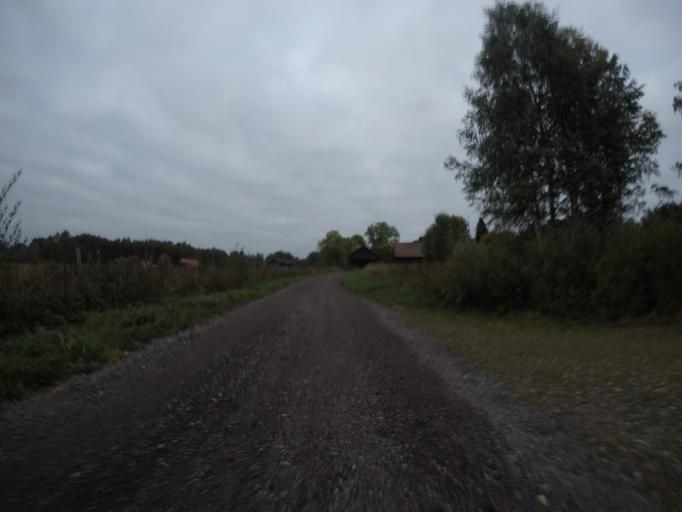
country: SE
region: Vaestmanland
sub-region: Kungsors Kommun
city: Kungsoer
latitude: 59.4018
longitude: 16.1172
